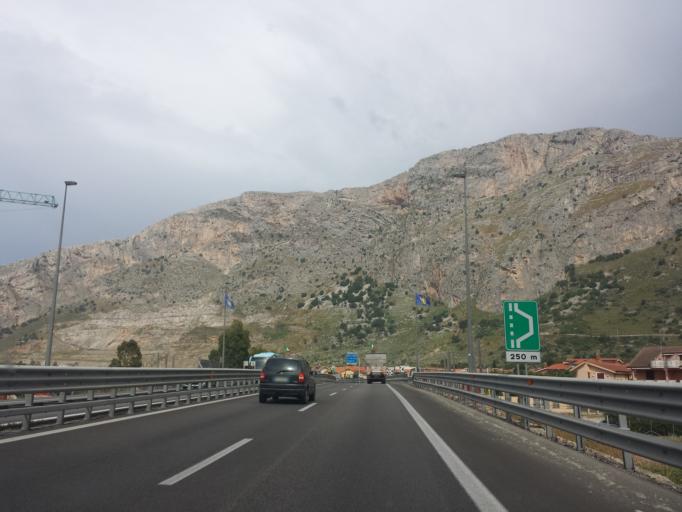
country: IT
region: Sicily
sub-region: Palermo
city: Isola delle Femmine
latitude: 38.1822
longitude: 13.2421
